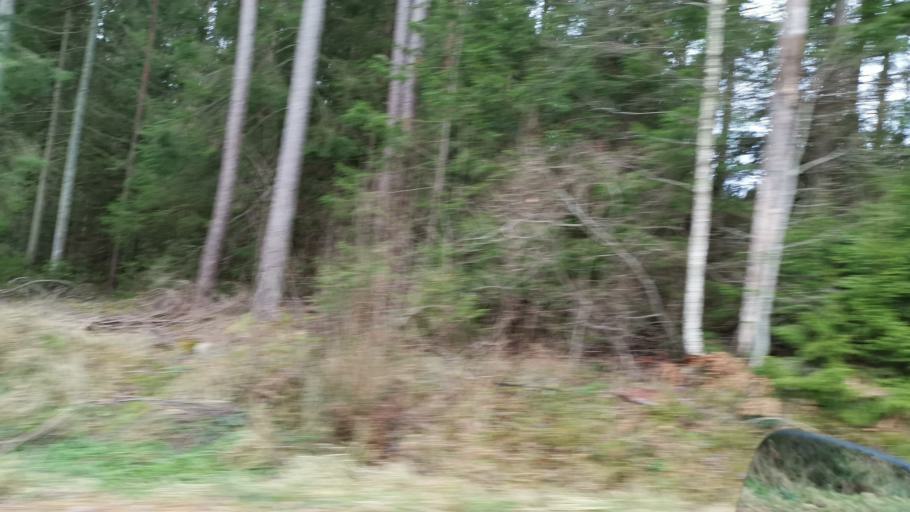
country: SE
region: Vaestra Goetaland
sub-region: Orust
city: Henan
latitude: 58.2202
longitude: 11.7086
